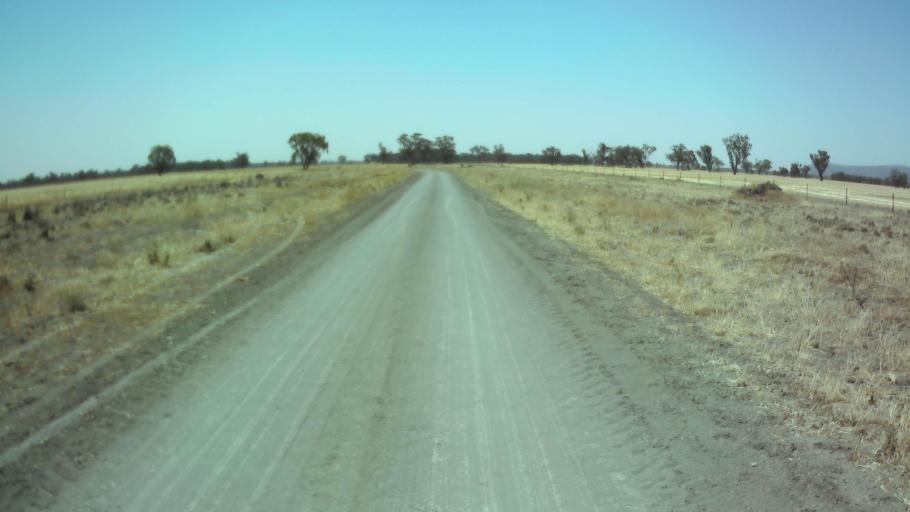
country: AU
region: New South Wales
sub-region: Weddin
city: Grenfell
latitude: -33.9943
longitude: 147.8652
